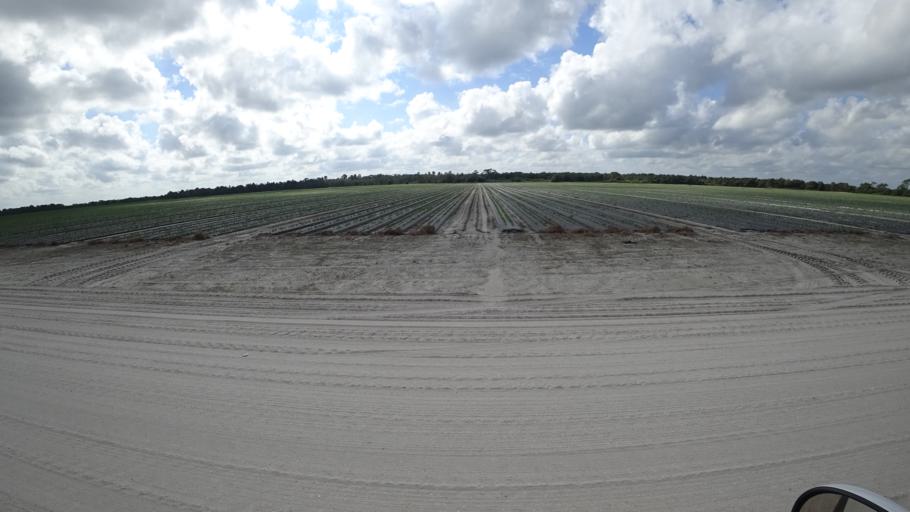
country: US
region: Florida
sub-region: Sarasota County
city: Lake Sarasota
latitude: 27.4132
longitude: -82.1912
